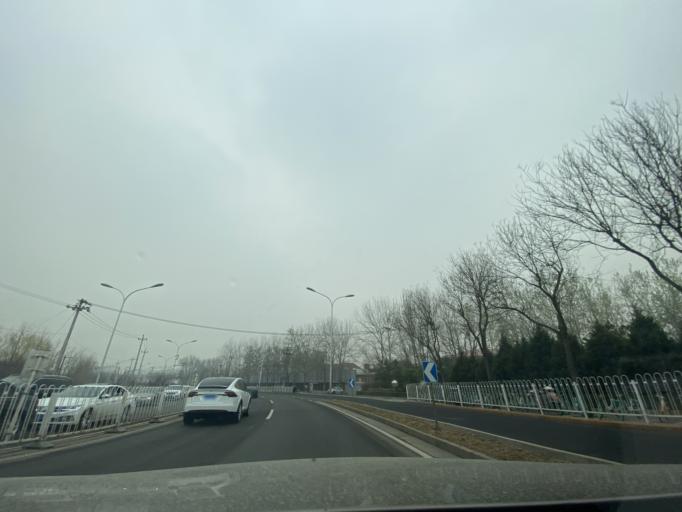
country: CN
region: Beijing
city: Sijiqing
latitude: 39.9689
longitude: 116.2592
